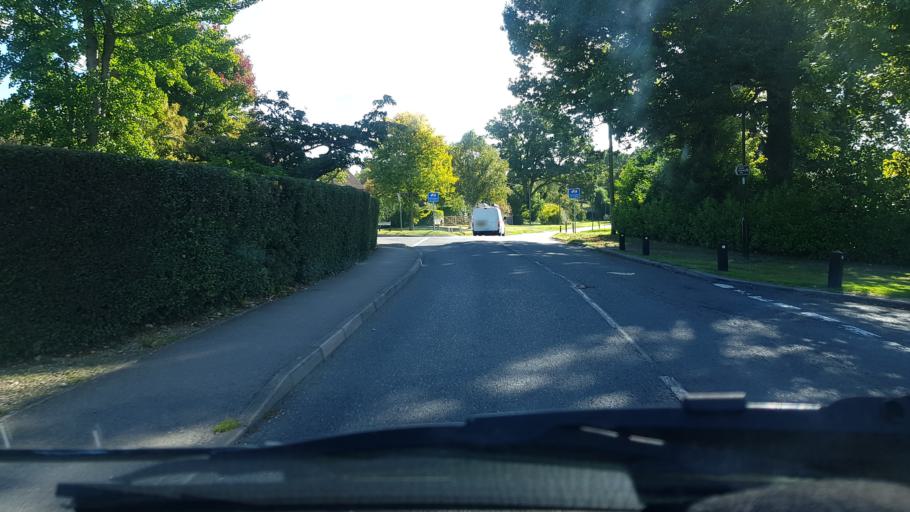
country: GB
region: England
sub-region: Surrey
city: Chiddingfold
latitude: 51.1107
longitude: -0.6269
